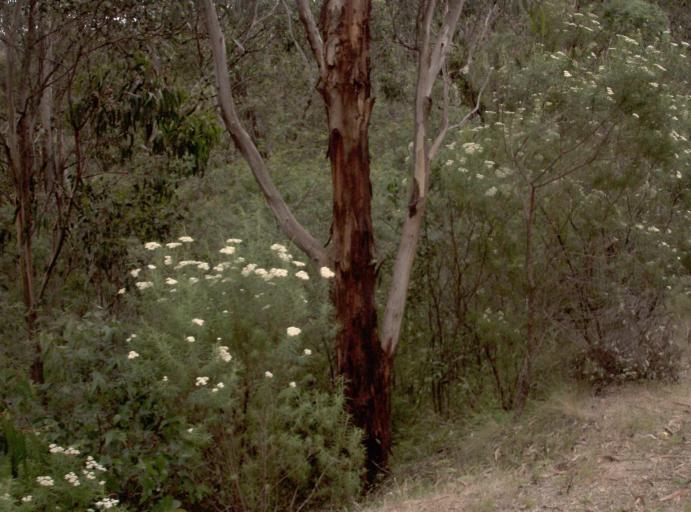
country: AU
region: Victoria
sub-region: East Gippsland
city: Bairnsdale
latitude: -37.6095
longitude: 147.1897
